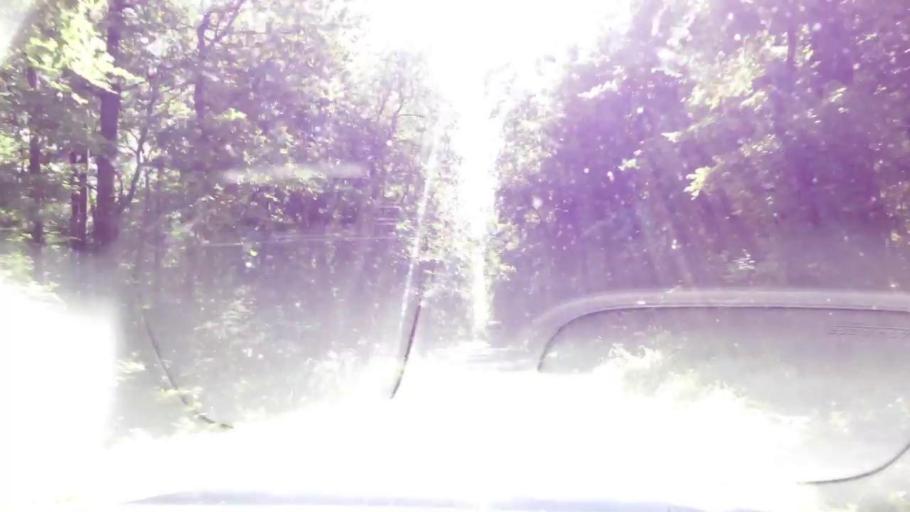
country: PL
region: West Pomeranian Voivodeship
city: Trzcinsko Zdroj
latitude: 52.8911
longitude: 14.6079
